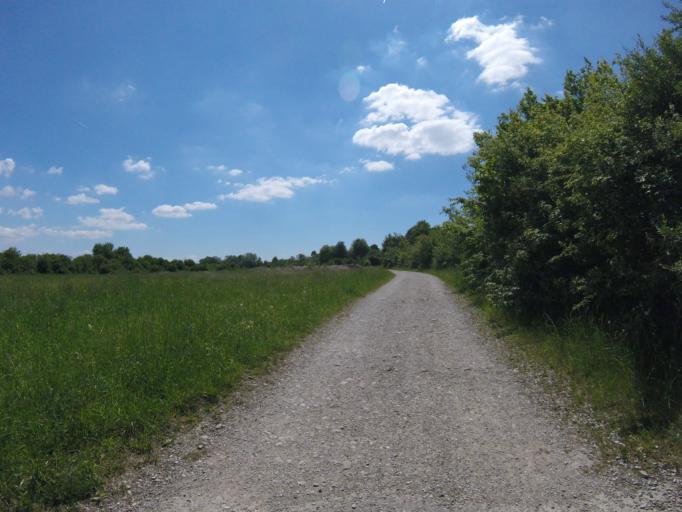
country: DE
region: Bavaria
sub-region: Upper Bavaria
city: Unterhaching
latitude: 48.0701
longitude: 11.6293
